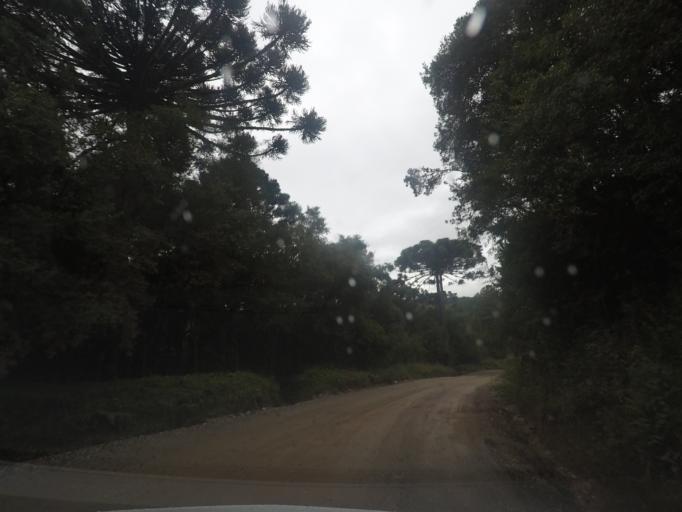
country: BR
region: Parana
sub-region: Campina Grande Do Sul
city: Campina Grande do Sul
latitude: -25.3085
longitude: -49.0965
